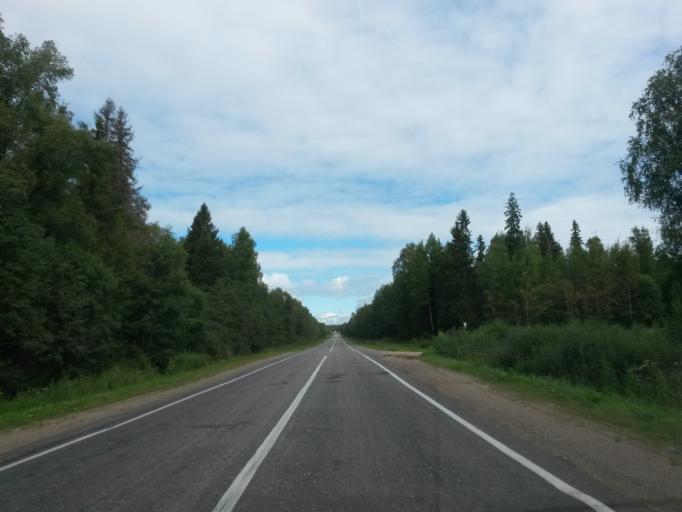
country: RU
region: Jaroslavl
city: Gavrilov-Yam
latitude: 57.4303
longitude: 39.9184
